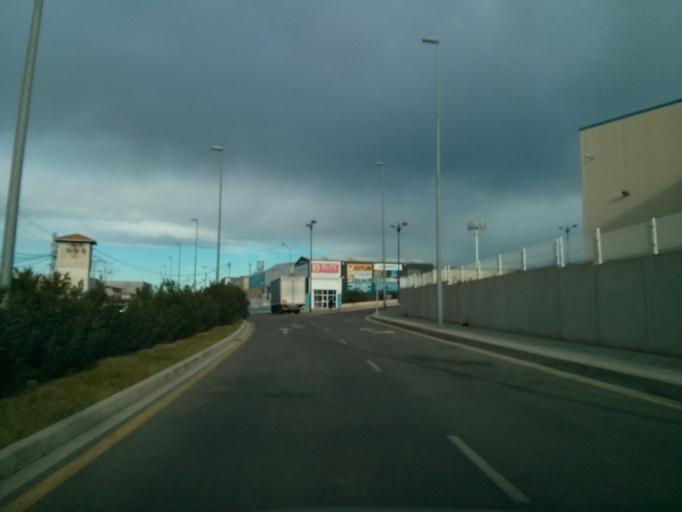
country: ES
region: Valencia
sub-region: Provincia de Valencia
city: Manises
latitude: 39.5210
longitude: -0.4628
